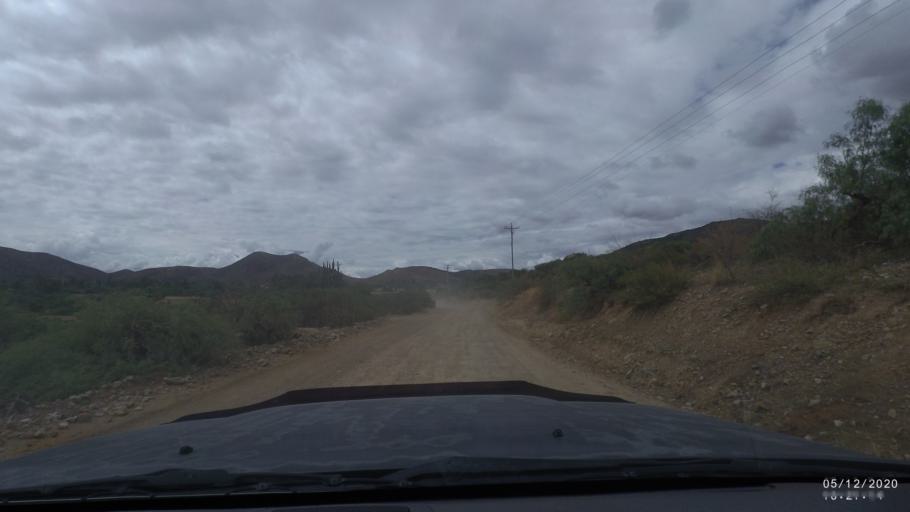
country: BO
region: Cochabamba
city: Sipe Sipe
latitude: -17.4883
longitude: -66.2821
